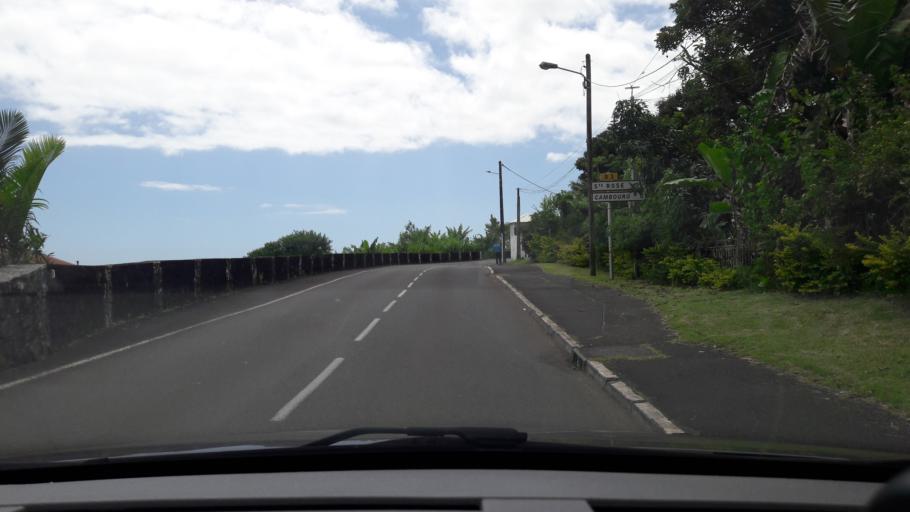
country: RE
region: Reunion
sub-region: Reunion
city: Saint-Benoit
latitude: -21.0817
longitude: 55.6932
